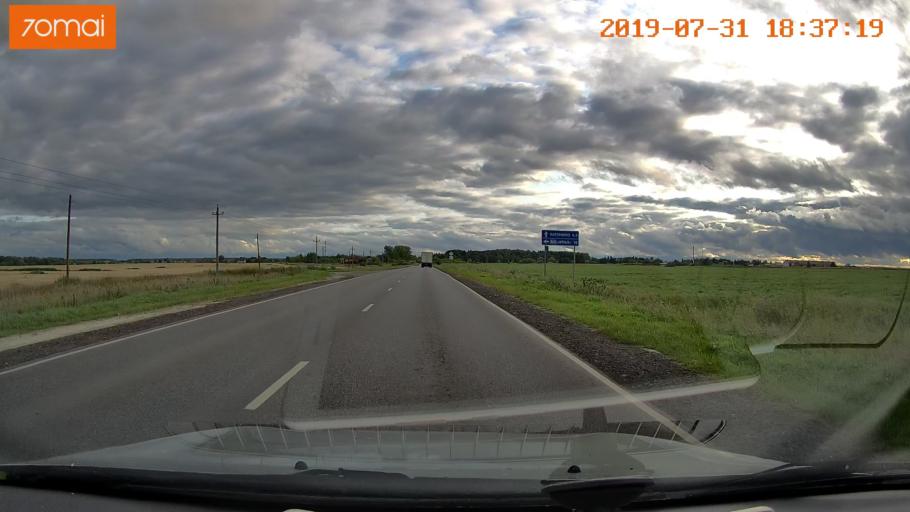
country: RU
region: Moskovskaya
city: Voskresensk
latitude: 55.2799
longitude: 38.6623
